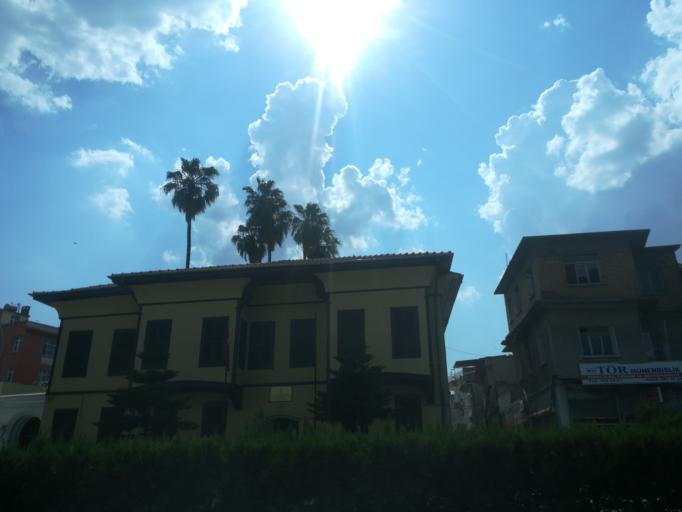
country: TR
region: Adana
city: Adana
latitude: 36.9888
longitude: 35.3319
